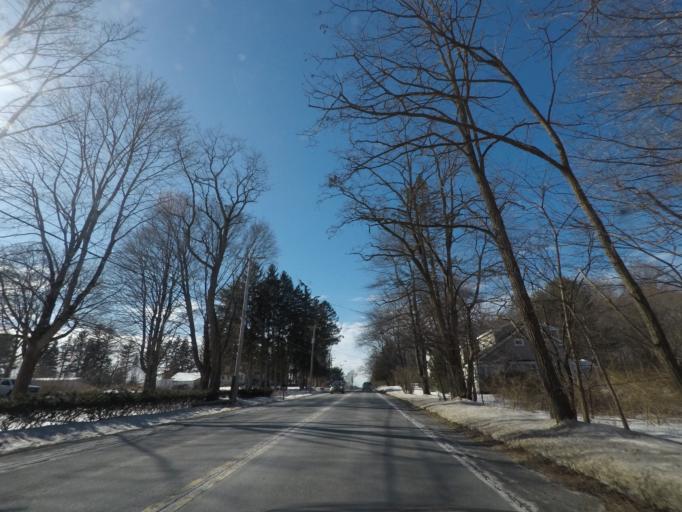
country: US
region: New York
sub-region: Albany County
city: Altamont
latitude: 42.7366
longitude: -73.9936
